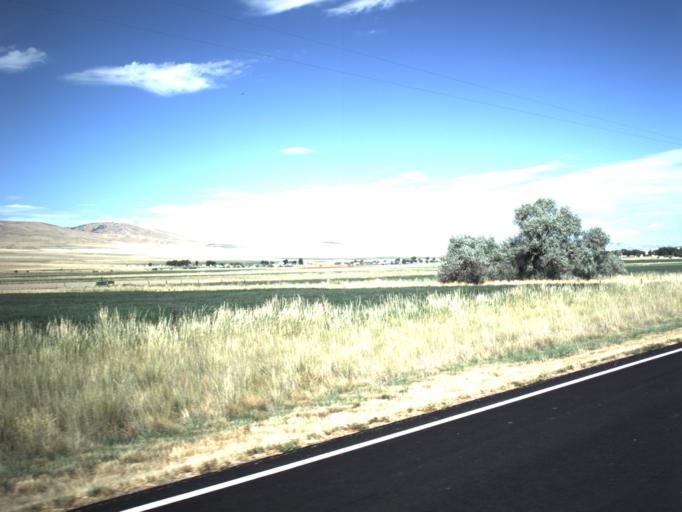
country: US
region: Utah
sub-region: Box Elder County
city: Garland
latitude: 41.7801
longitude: -112.4352
